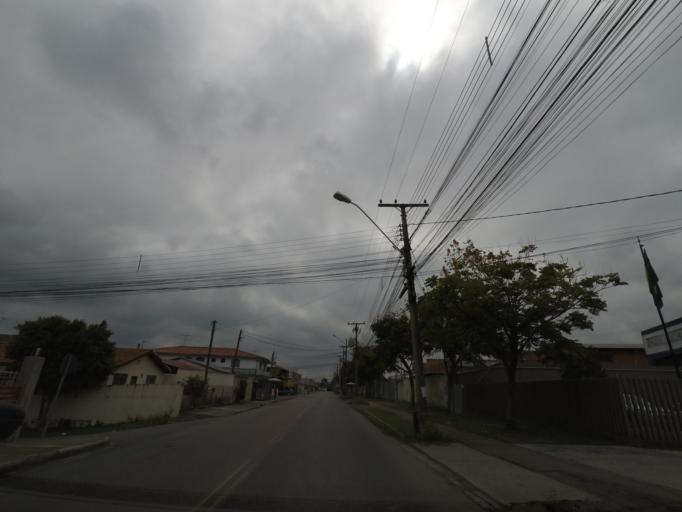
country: BR
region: Parana
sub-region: Curitiba
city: Curitiba
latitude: -25.5065
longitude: -49.3346
